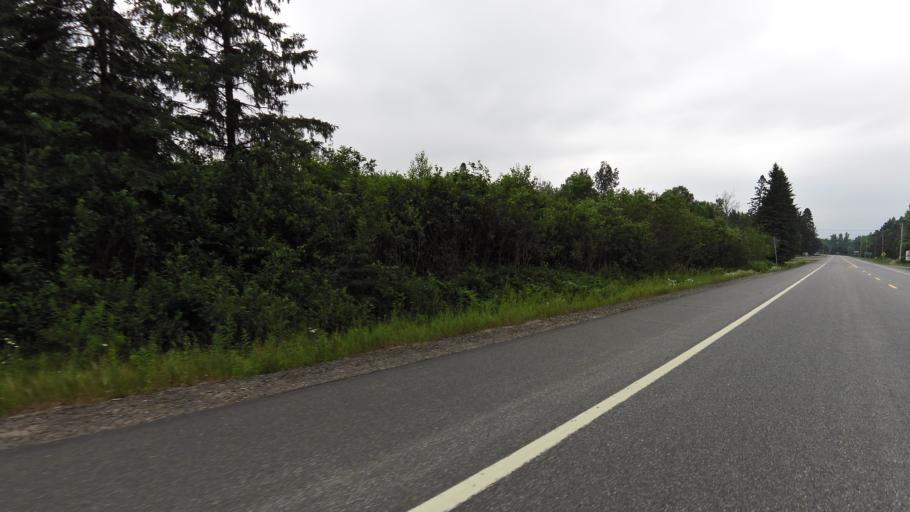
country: CA
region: Ontario
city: Huntsville
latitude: 45.3638
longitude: -78.9286
